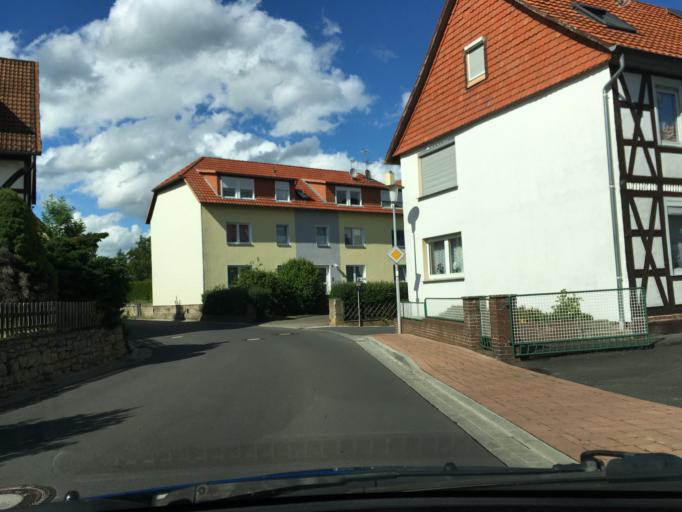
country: DE
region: Lower Saxony
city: Hardegsen
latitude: 51.6206
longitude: 9.8511
